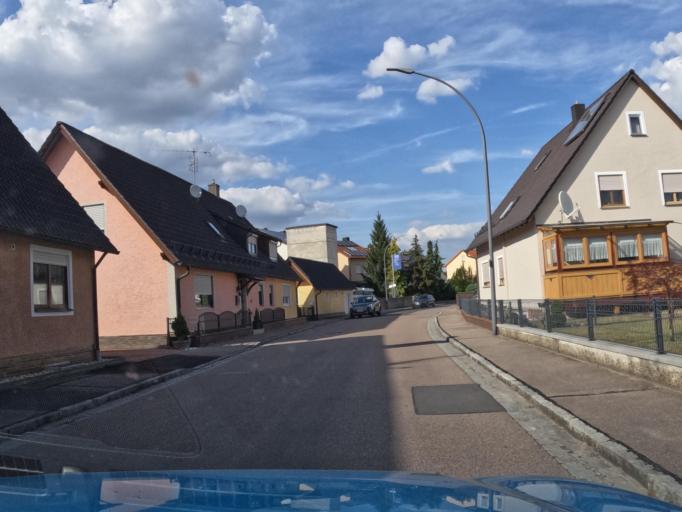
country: DE
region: Bavaria
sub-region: Upper Palatinate
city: Schwarzenfeld
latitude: 49.3864
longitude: 12.1239
